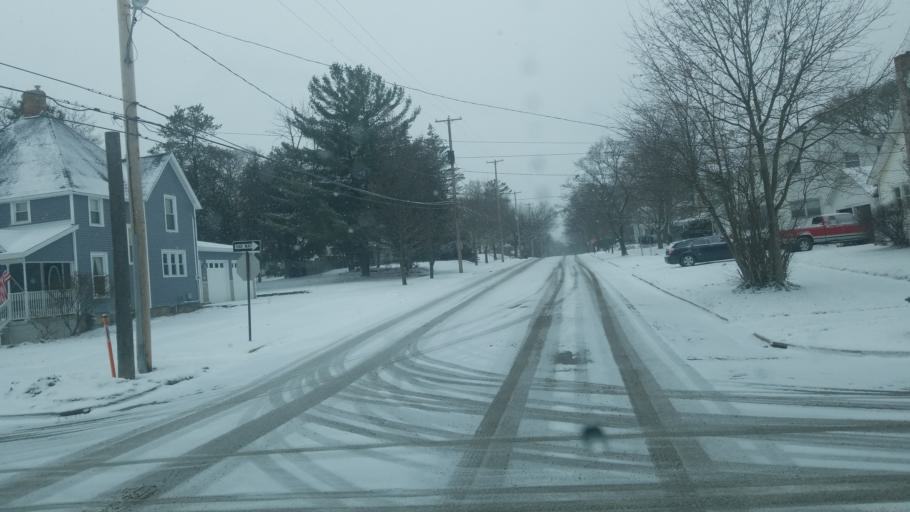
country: US
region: Michigan
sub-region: Mecosta County
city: Big Rapids
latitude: 43.6944
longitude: -85.4774
